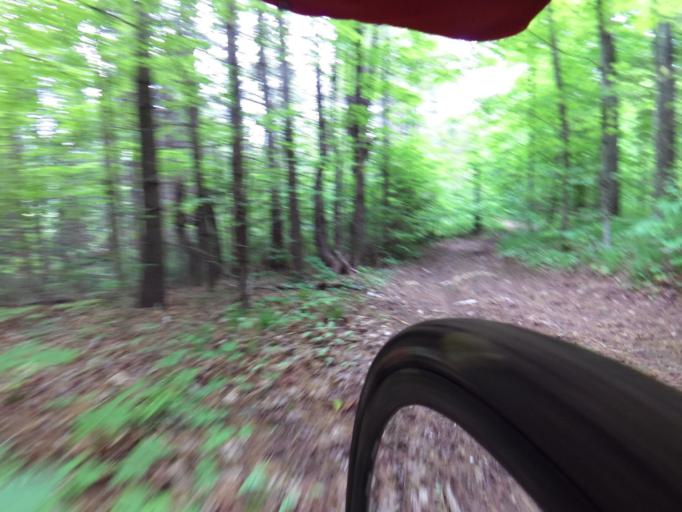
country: CA
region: Ontario
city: Arnprior
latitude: 45.1866
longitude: -76.5313
